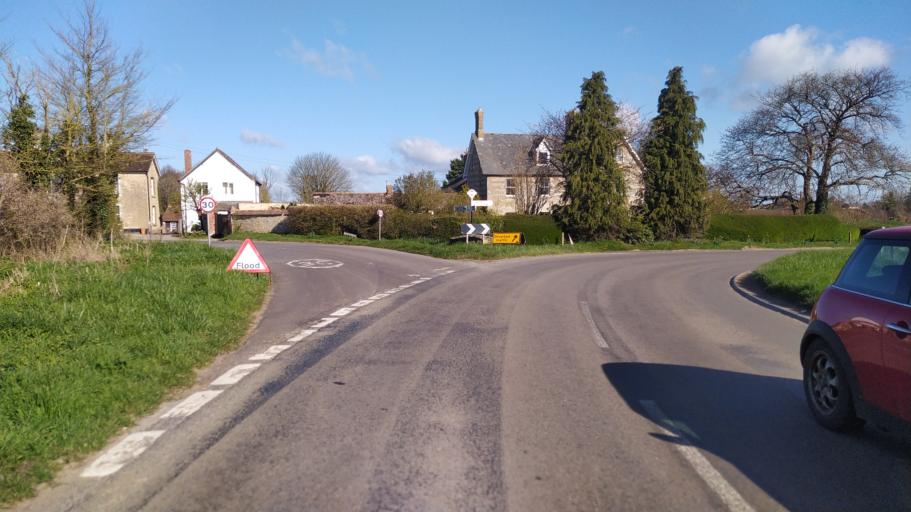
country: GB
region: England
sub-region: Dorset
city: Sturminster Newton
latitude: 50.9586
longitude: -2.3137
